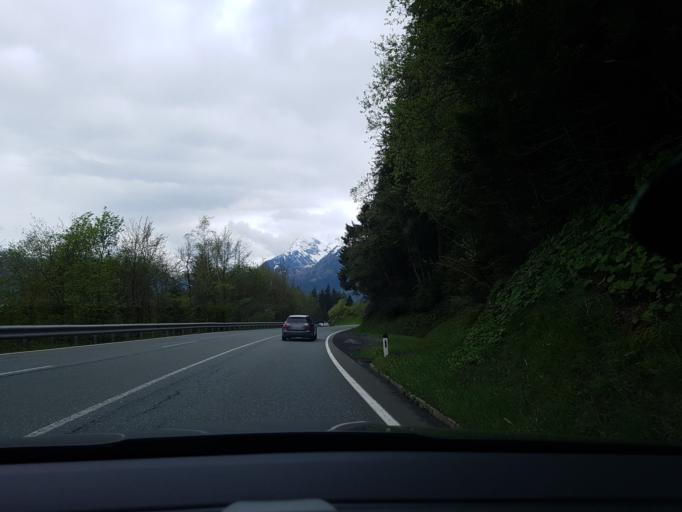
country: AT
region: Salzburg
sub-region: Politischer Bezirk Zell am See
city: Hollersbach im Pinzgau
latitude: 47.3045
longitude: 12.4114
